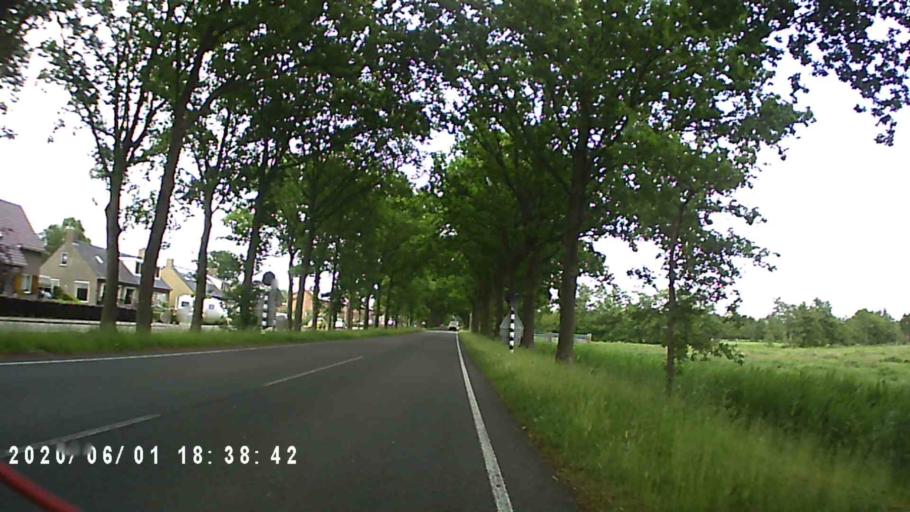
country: NL
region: Friesland
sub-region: Gemeente Tytsjerksteradiel
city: Eastermar
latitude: 53.1732
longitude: 6.0576
